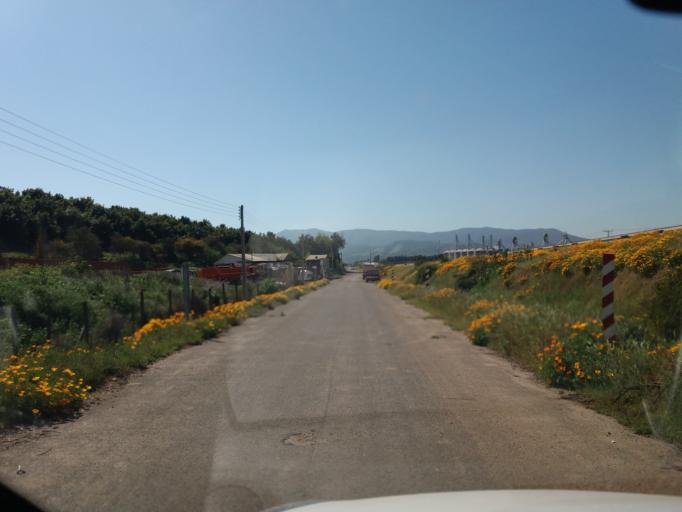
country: CL
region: Valparaiso
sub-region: Provincia de Marga Marga
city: Limache
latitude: -32.9482
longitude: -71.2857
